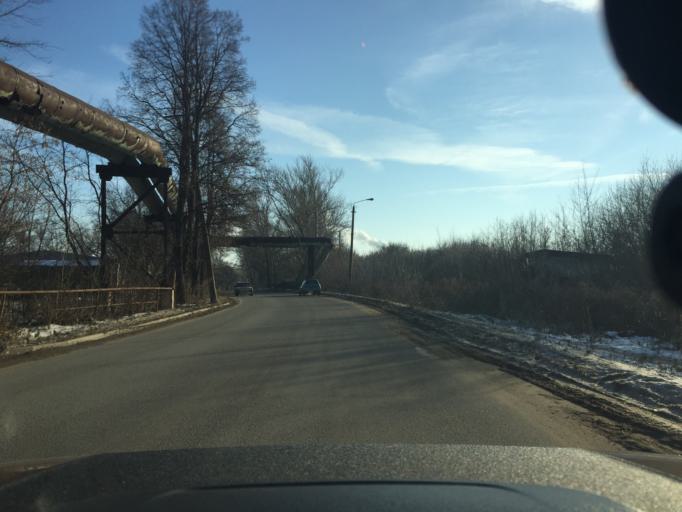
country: RU
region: Tula
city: Tula
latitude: 54.1758
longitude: 37.7019
